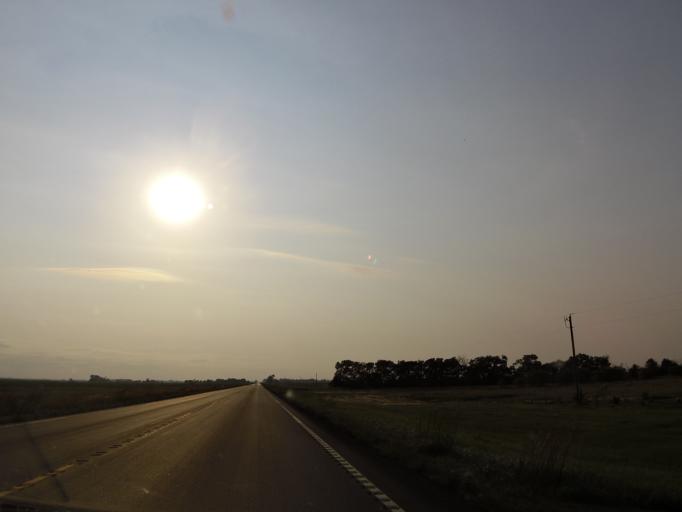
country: US
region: North Dakota
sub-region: Traill County
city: Mayville
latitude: 47.3529
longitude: -97.2636
